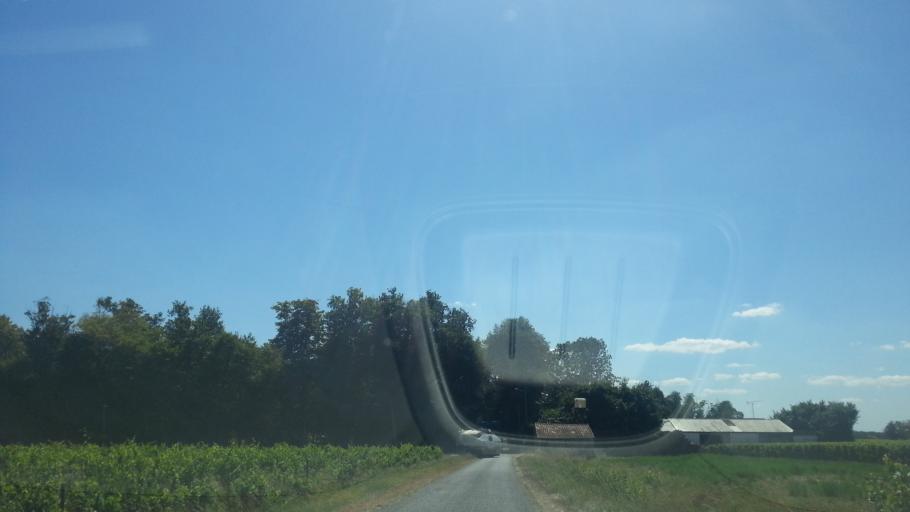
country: FR
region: Aquitaine
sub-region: Departement de la Gironde
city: Landiras
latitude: 44.5699
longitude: -0.3979
